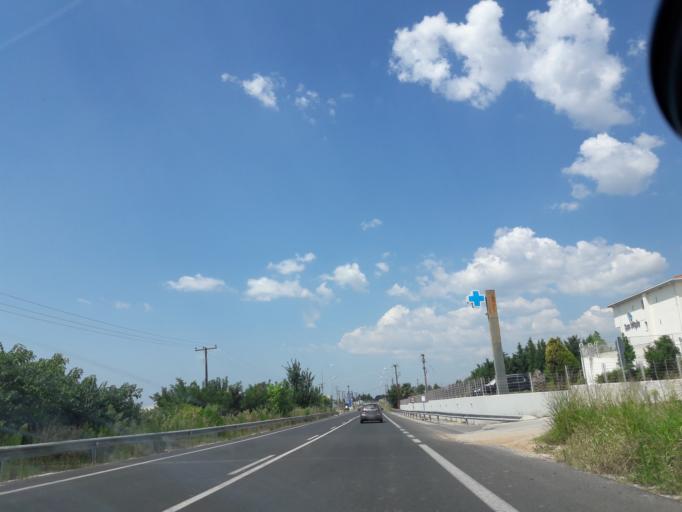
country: GR
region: Central Macedonia
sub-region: Nomos Thessalonikis
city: Agia Paraskevi
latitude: 40.5161
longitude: 23.0691
